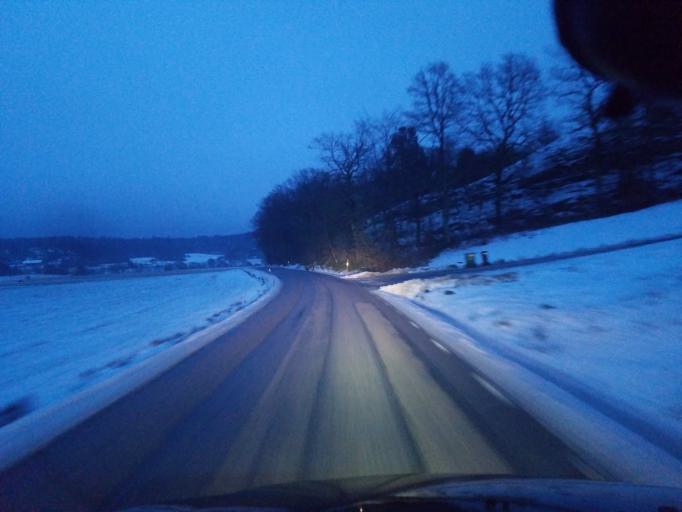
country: SE
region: Vaestra Goetaland
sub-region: Orust
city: Henan
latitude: 58.2803
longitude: 11.5884
